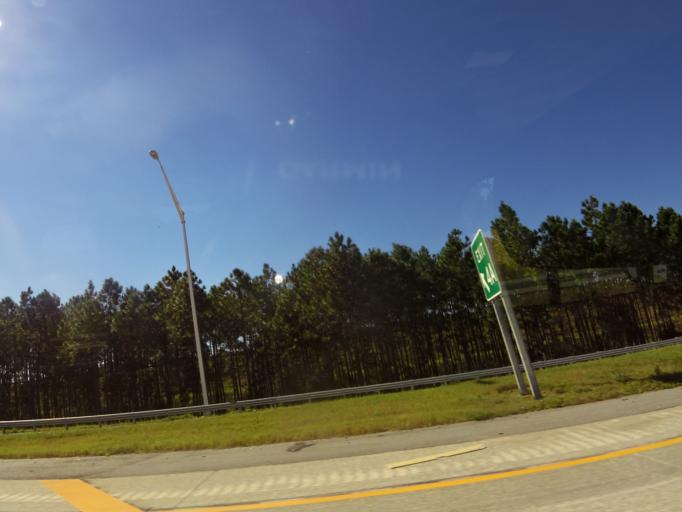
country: US
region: Florida
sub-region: Saint Johns County
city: Fruit Cove
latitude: 30.1169
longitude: -81.5133
